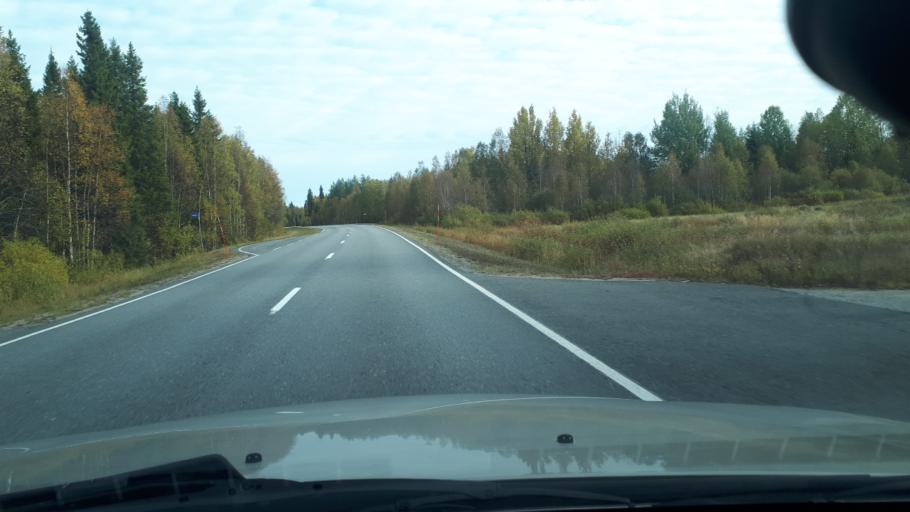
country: FI
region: Lapland
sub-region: Rovaniemi
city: Rovaniemi
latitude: 65.9584
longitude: 25.9411
